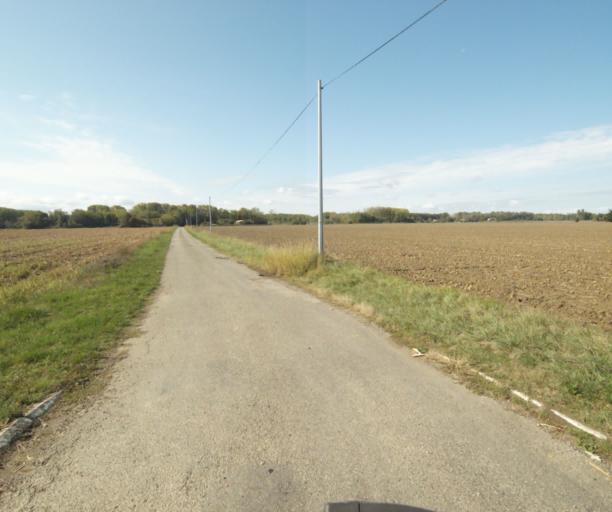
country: FR
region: Midi-Pyrenees
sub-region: Departement du Tarn-et-Garonne
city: Verdun-sur-Garonne
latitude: 43.8787
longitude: 1.2340
